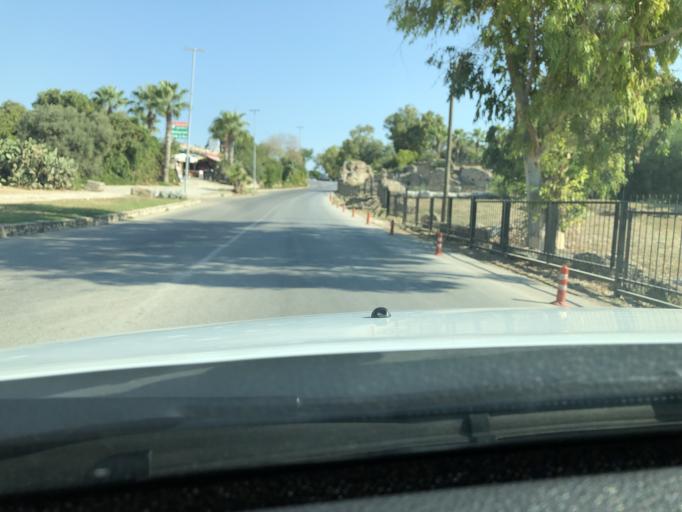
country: TR
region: Antalya
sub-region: Manavgat
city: Side
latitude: 36.7714
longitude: 31.3945
